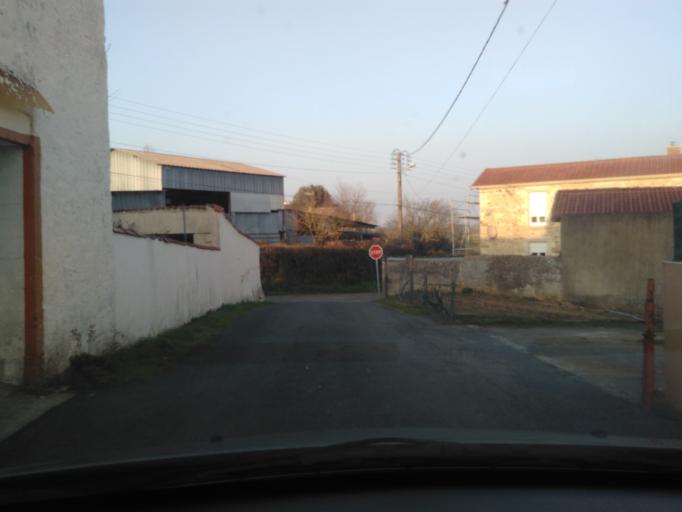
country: FR
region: Pays de la Loire
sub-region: Departement de la Vendee
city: Chantonnay
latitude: 46.6618
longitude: -1.0125
